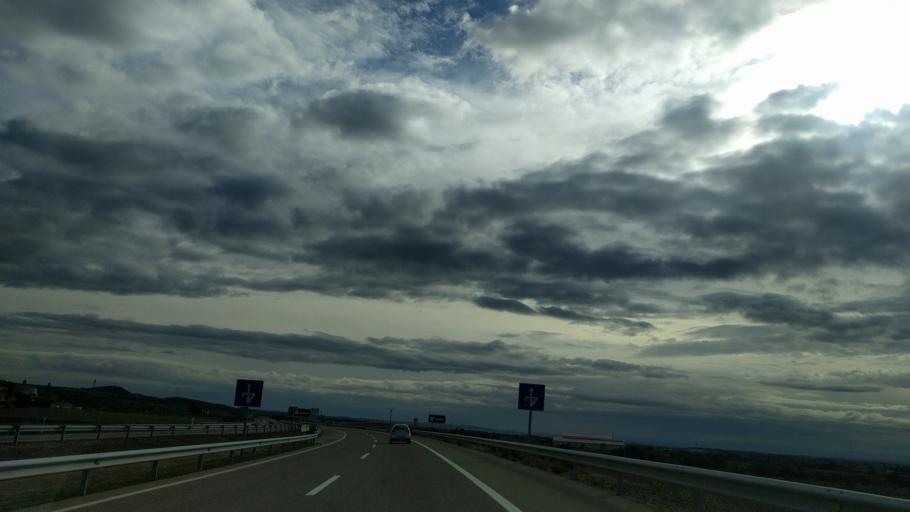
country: ES
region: Aragon
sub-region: Provincia de Huesca
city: Igries
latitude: 42.2189
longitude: -0.4421
